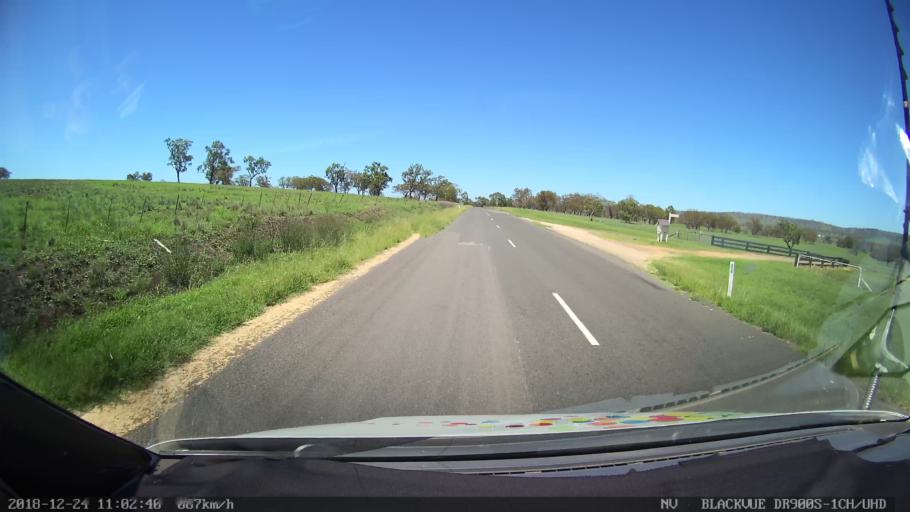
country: AU
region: New South Wales
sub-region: Upper Hunter Shire
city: Merriwa
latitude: -32.0875
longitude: 150.3732
